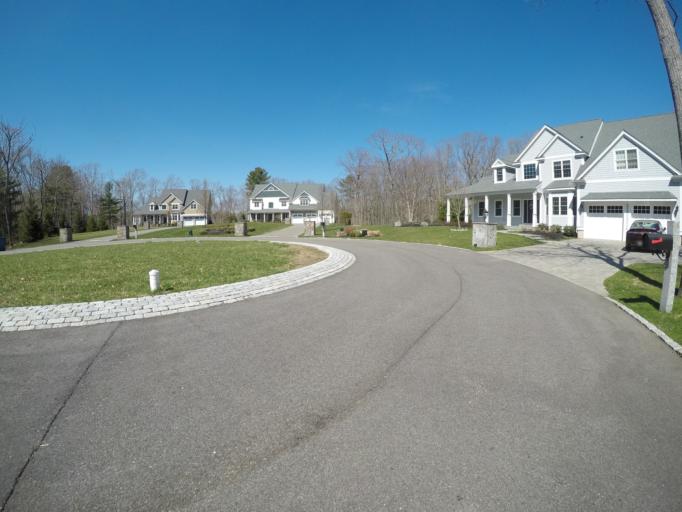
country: US
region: Massachusetts
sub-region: Norfolk County
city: Stoughton
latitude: 42.0906
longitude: -71.0819
